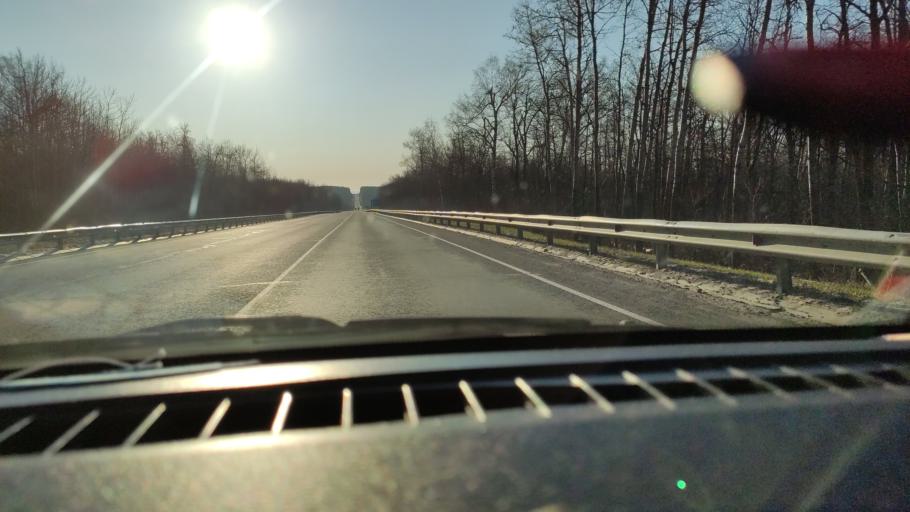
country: RU
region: Saratov
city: Vol'sk
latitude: 52.1097
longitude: 47.3677
